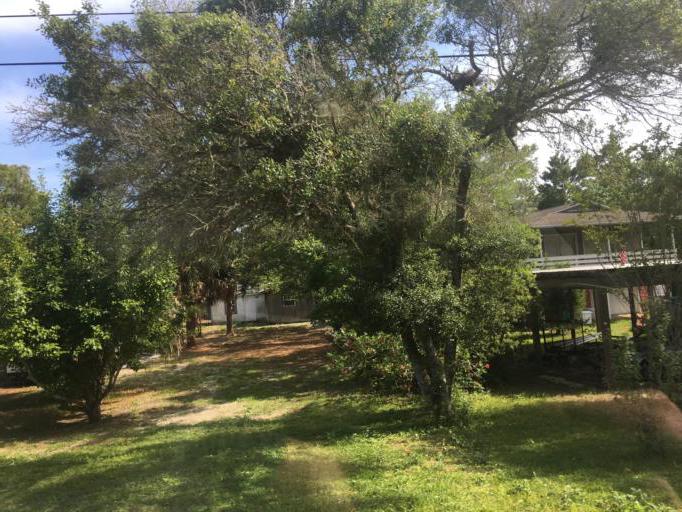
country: US
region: Florida
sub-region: Bay County
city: Laguna Beach
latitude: 30.2663
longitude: -85.9649
